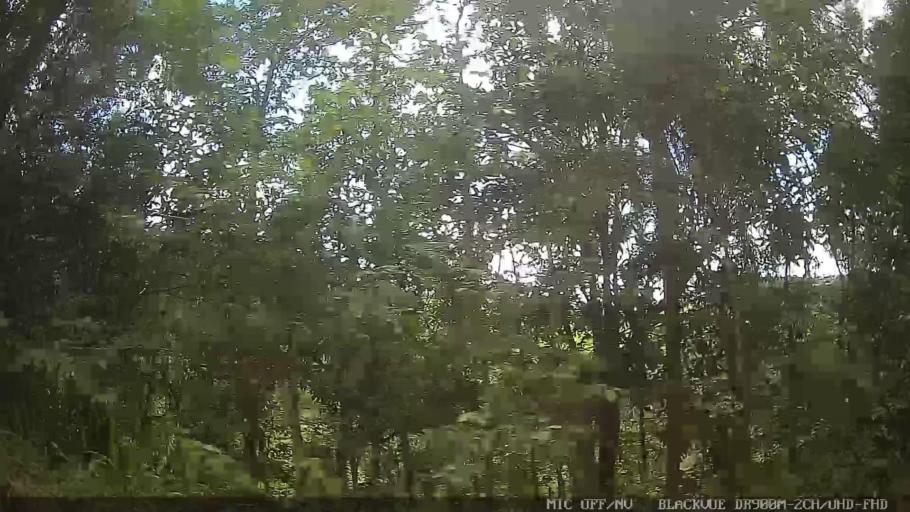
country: BR
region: Sao Paulo
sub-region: Atibaia
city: Atibaia
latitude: -23.1579
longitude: -46.6412
